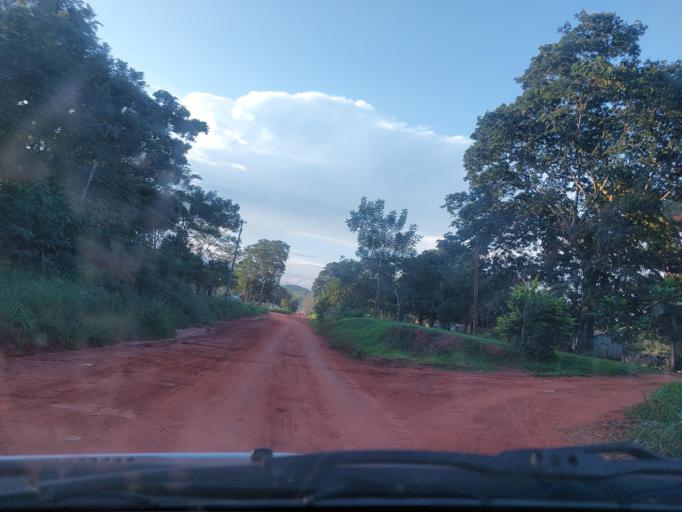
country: PY
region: San Pedro
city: Lima
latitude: -24.1425
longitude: -56.0113
